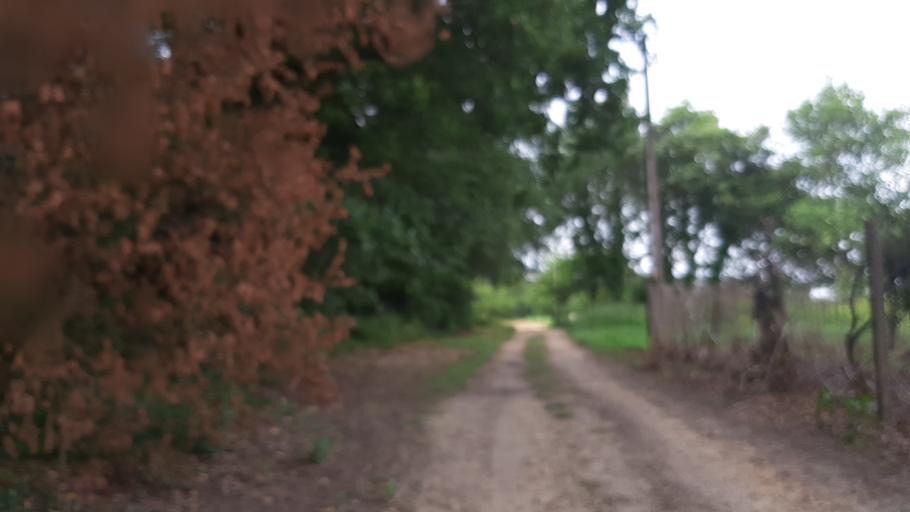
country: ES
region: Galicia
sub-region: Provincia de Pontevedra
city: O Rosal
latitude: 41.9242
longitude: -8.8264
